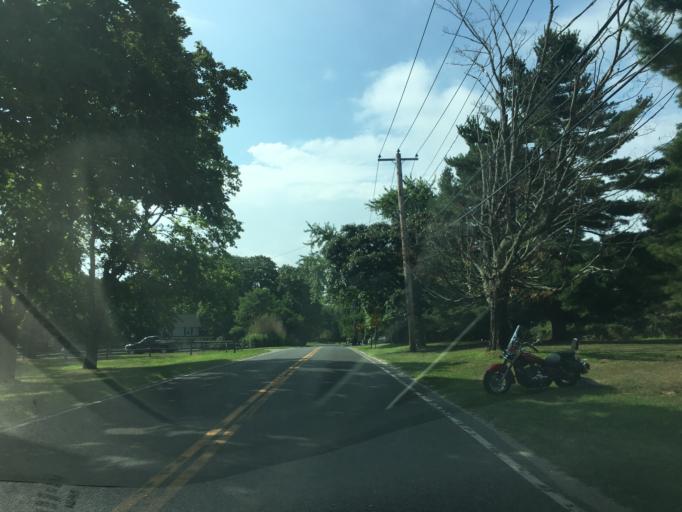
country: US
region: New York
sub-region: Suffolk County
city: Shelter Island
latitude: 41.0659
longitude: -72.3312
